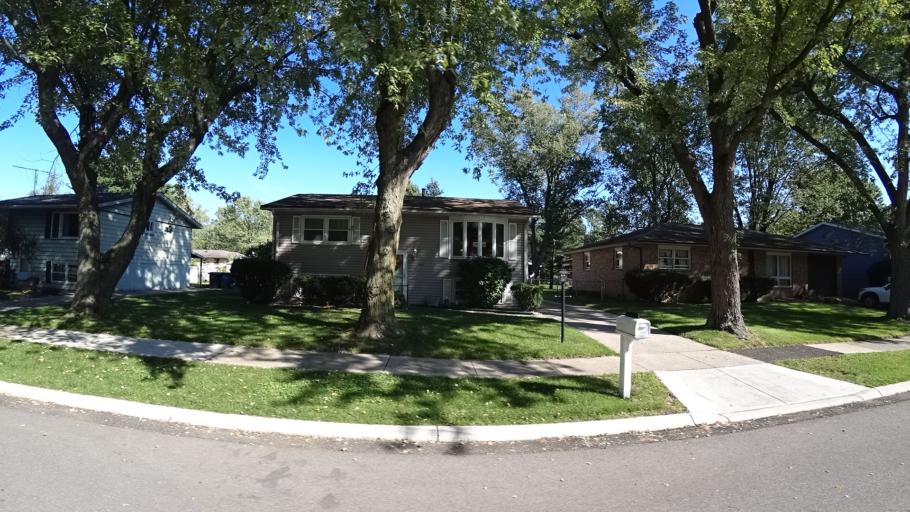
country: US
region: Indiana
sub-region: LaPorte County
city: Michigan City
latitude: 41.6898
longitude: -86.9078
